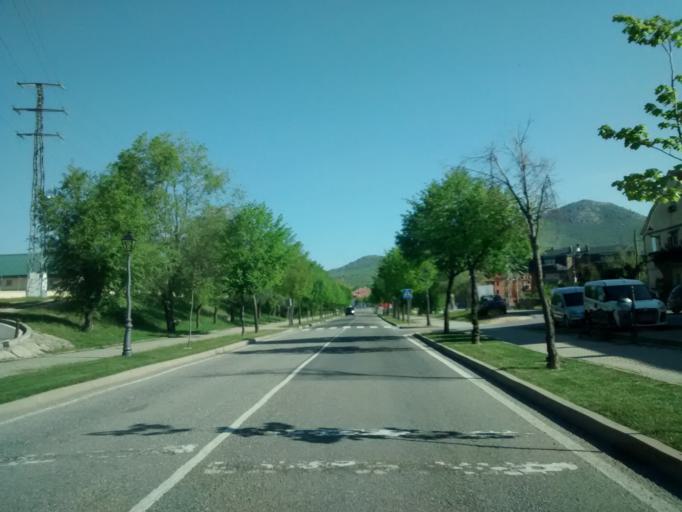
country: ES
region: Castille and Leon
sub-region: Provincia de Segovia
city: San Ildefonso
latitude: 40.9062
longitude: -4.0091
